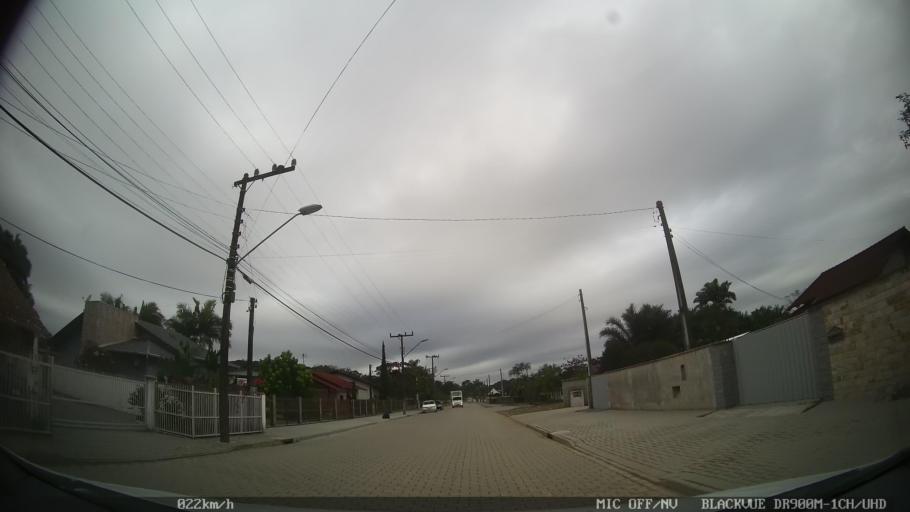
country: BR
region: Santa Catarina
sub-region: Joinville
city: Joinville
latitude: -26.2661
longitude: -48.9263
